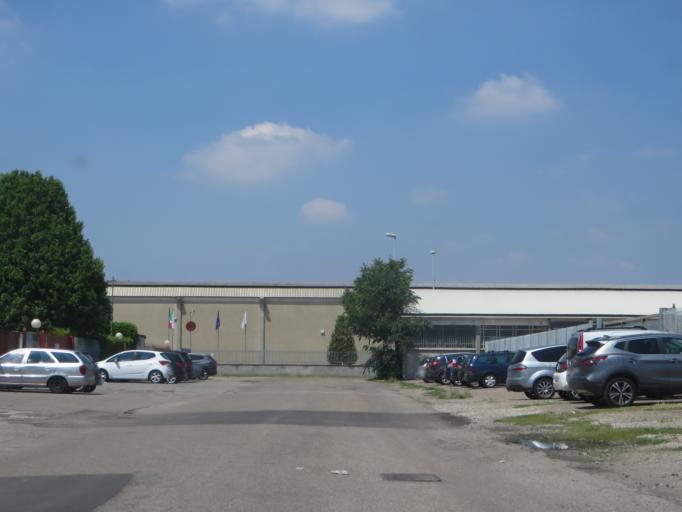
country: IT
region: Lombardy
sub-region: Citta metropolitana di Milano
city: Bareggio
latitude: 45.4938
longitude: 8.9921
